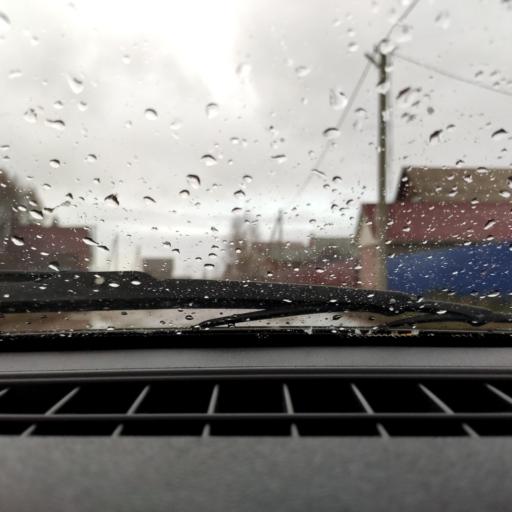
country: RU
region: Bashkortostan
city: Iglino
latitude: 54.7360
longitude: 56.3257
